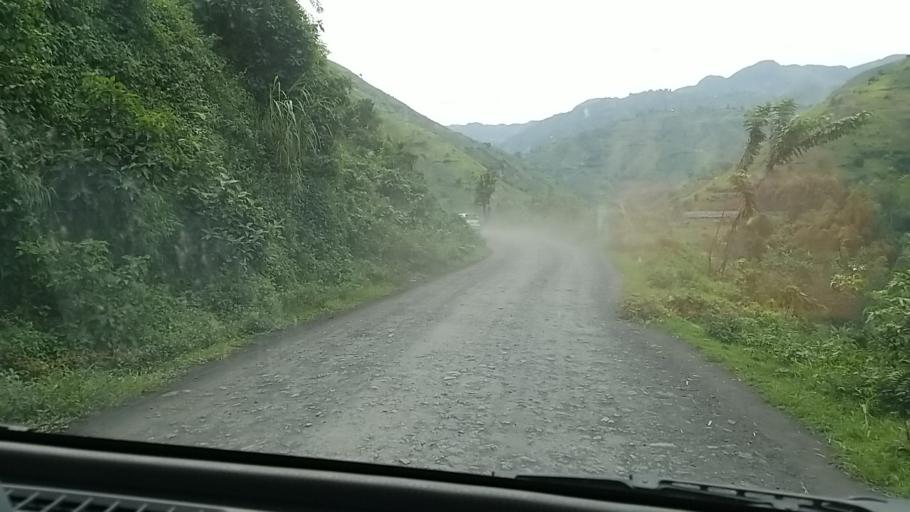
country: CD
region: Nord Kivu
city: Sake
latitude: -1.7423
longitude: 28.9922
